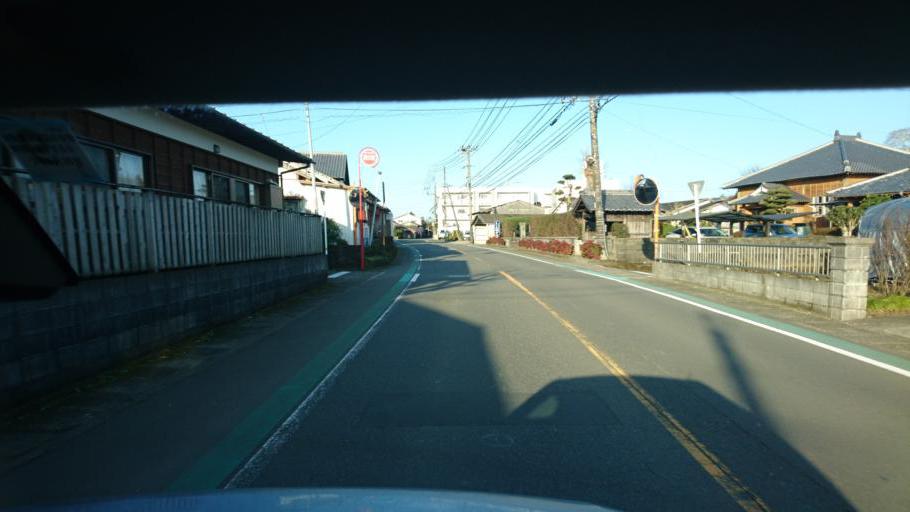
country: JP
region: Miyazaki
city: Miyazaki-shi
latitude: 31.8437
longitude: 131.4053
